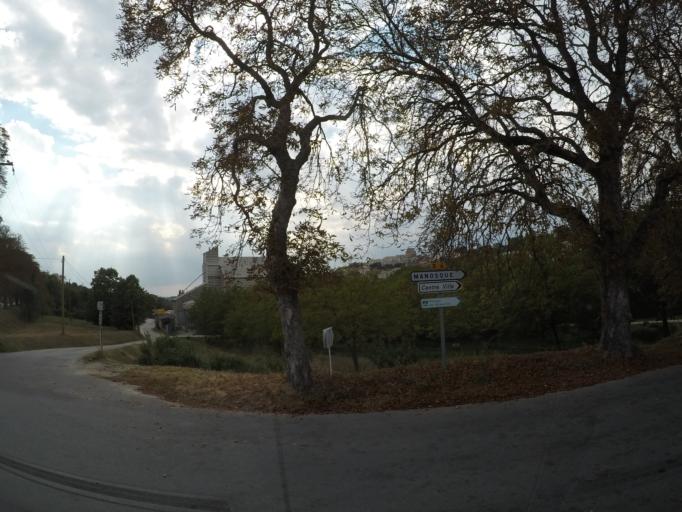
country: FR
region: Provence-Alpes-Cote d'Azur
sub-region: Departement des Alpes-de-Haute-Provence
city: Valensole
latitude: 43.8379
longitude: 5.9912
